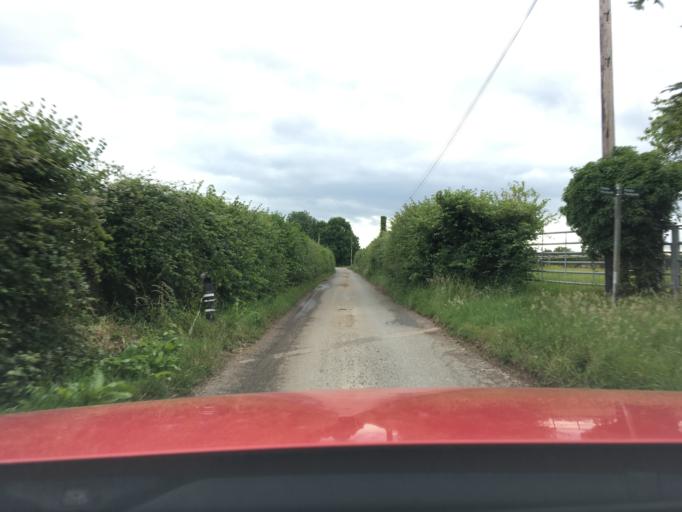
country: GB
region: England
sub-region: Gloucestershire
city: Cinderford
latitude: 51.7944
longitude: -2.4070
